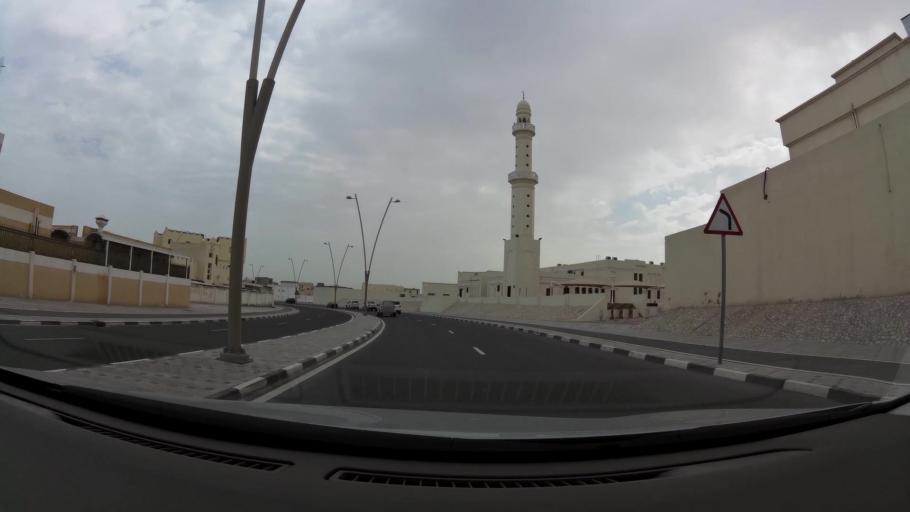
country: QA
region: Baladiyat ad Dawhah
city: Doha
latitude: 25.3468
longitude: 51.4883
